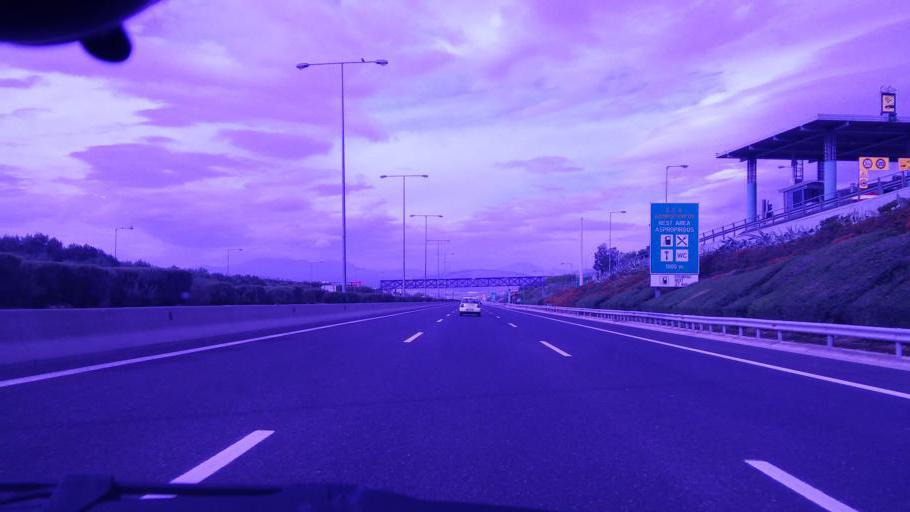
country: GR
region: Attica
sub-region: Nomarchia Dytikis Attikis
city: Aspropyrgos
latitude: 38.0901
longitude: 23.6206
